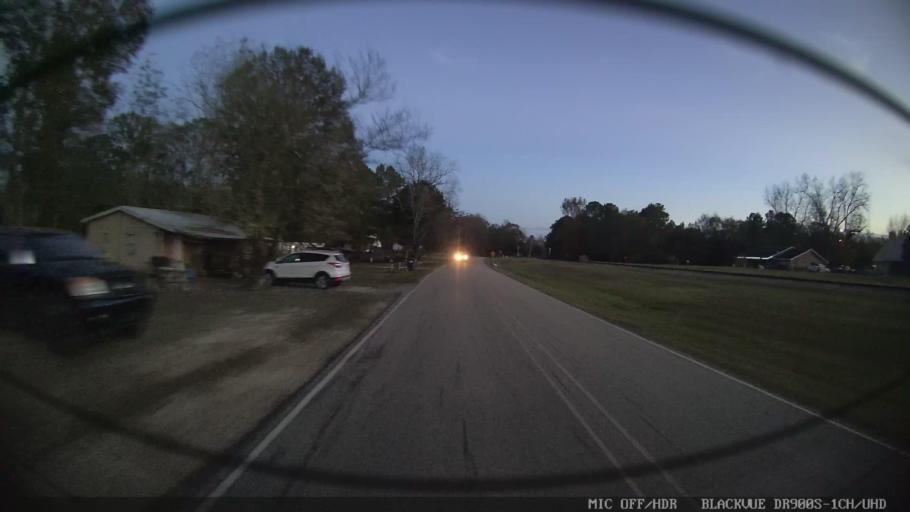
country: US
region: Mississippi
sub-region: Forrest County
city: Hattiesburg
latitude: 31.1667
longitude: -89.2154
